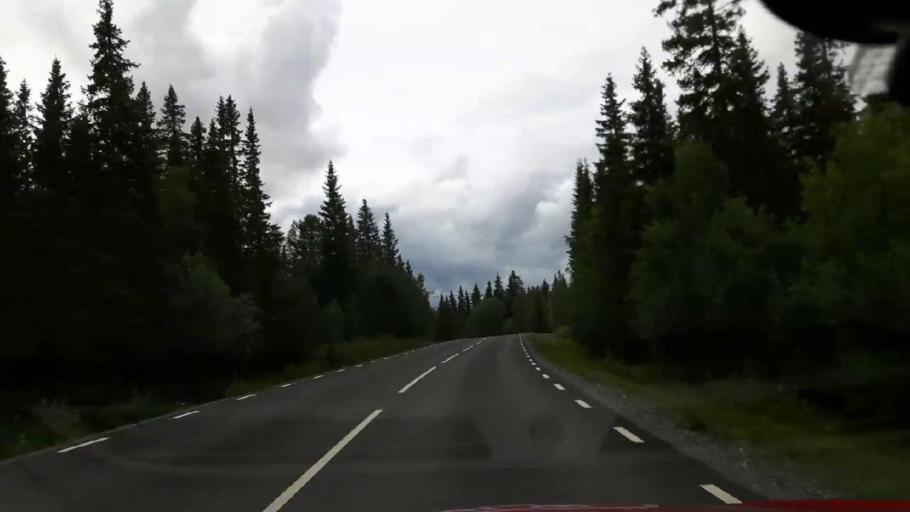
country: NO
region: Nord-Trondelag
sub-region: Lierne
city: Sandvika
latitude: 64.5958
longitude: 14.1177
